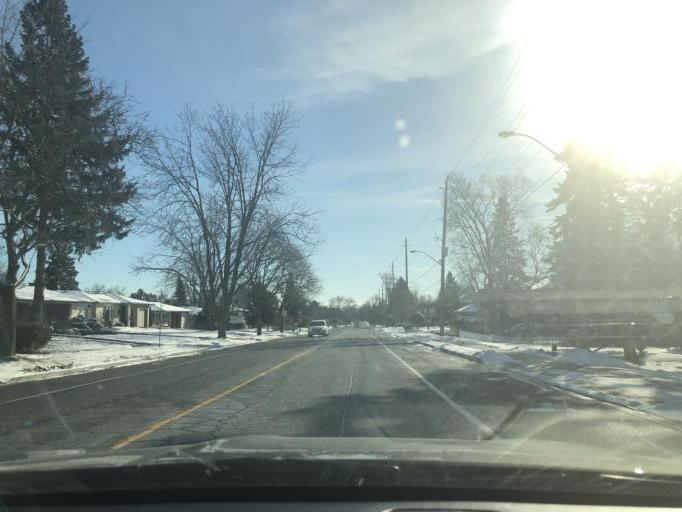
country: CA
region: Ontario
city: Scarborough
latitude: 43.7807
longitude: -79.1478
